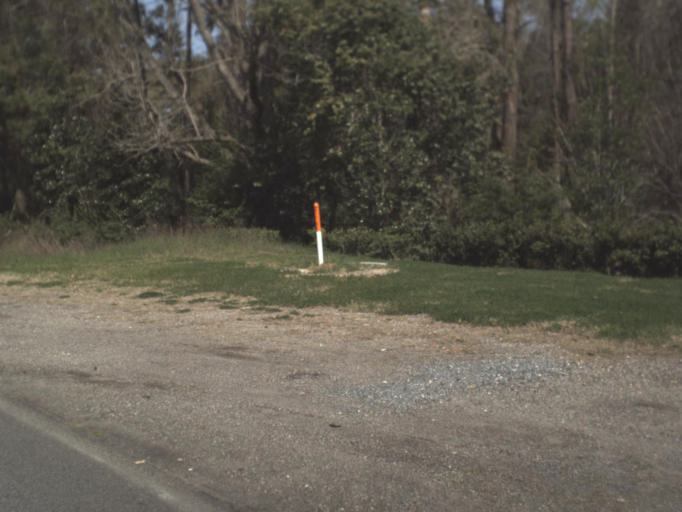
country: US
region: Florida
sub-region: Leon County
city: Tallahassee
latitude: 30.4888
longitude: -84.3205
